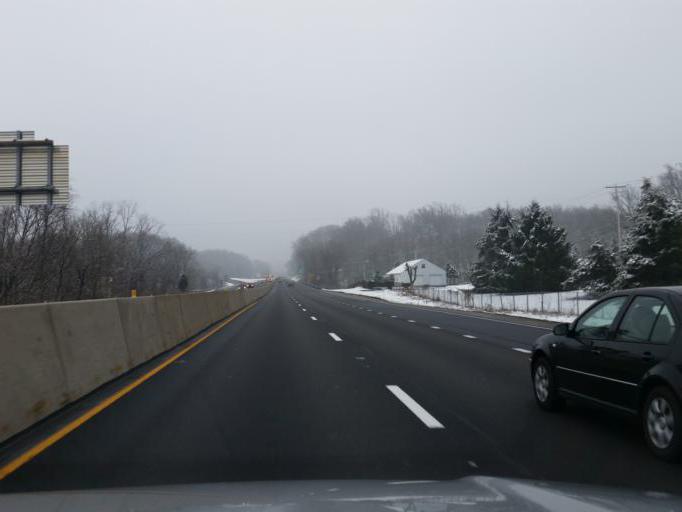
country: US
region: Pennsylvania
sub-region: York County
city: Valley Green
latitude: 40.1435
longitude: -76.8122
